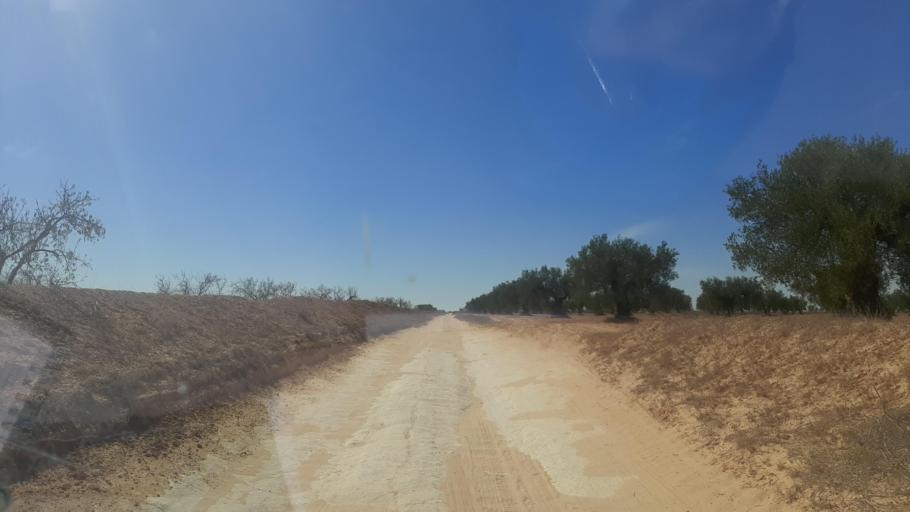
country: TN
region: Safaqis
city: Sfax
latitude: 34.8178
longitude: 10.5501
